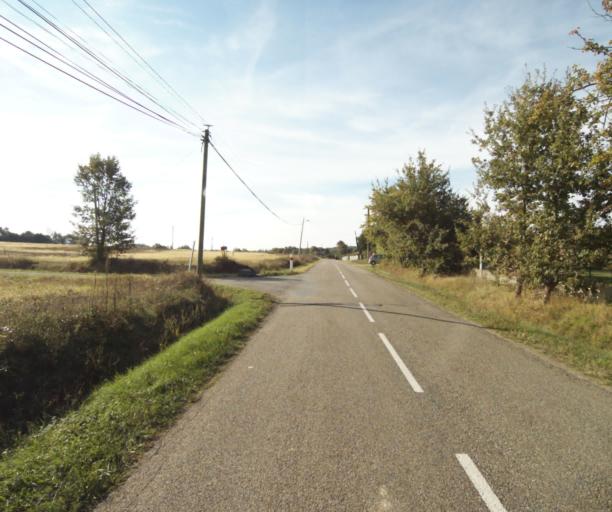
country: FR
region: Midi-Pyrenees
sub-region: Departement du Tarn-et-Garonne
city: Nohic
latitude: 43.9272
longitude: 1.4640
